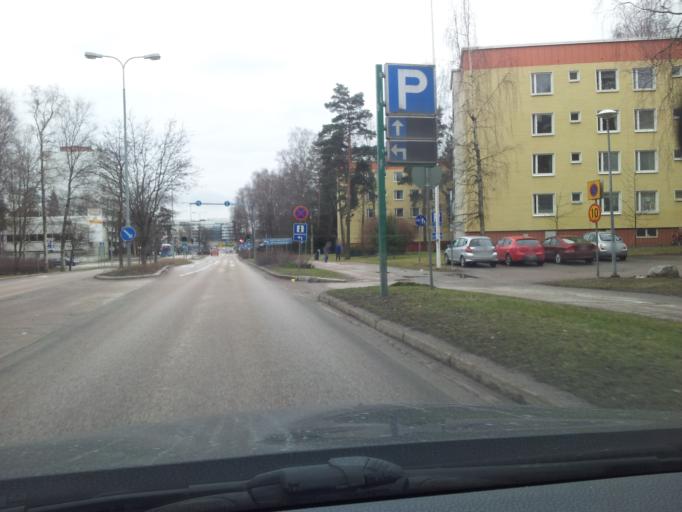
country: FI
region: Uusimaa
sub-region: Helsinki
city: Otaniemi
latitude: 60.1776
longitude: 24.7993
